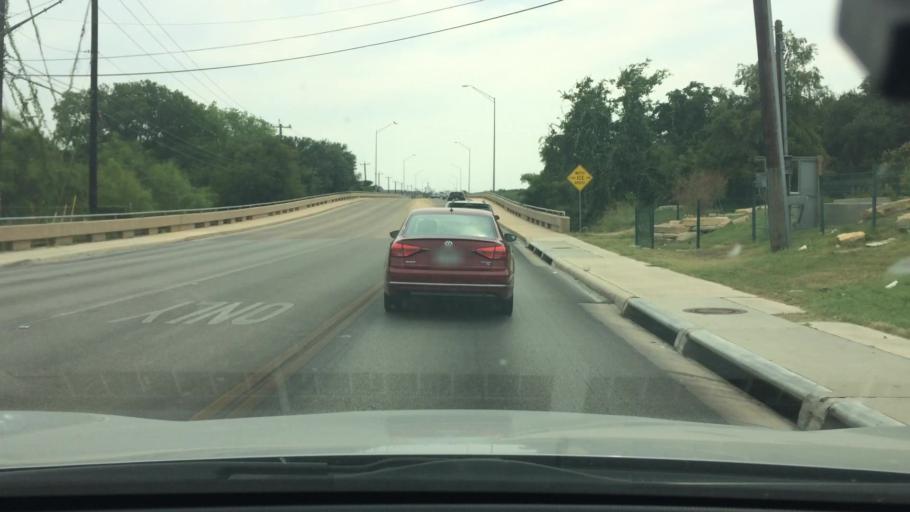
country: US
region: Texas
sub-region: Bexar County
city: Leon Valley
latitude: 29.4645
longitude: -98.6253
